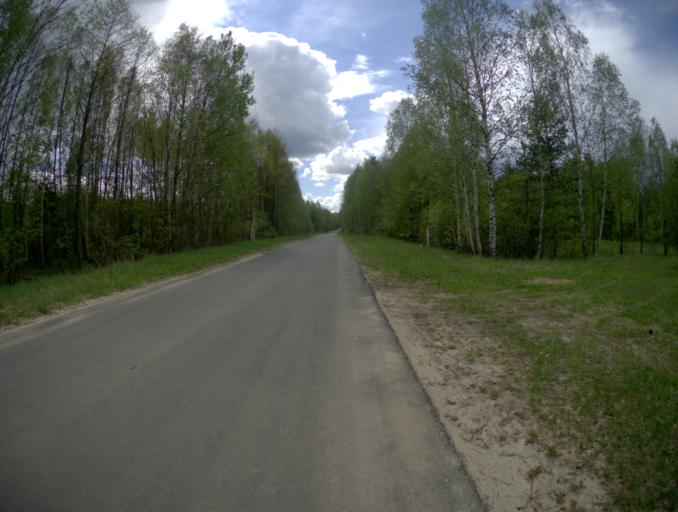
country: RU
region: Vladimir
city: Velikodvorskiy
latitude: 55.2542
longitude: 40.7749
